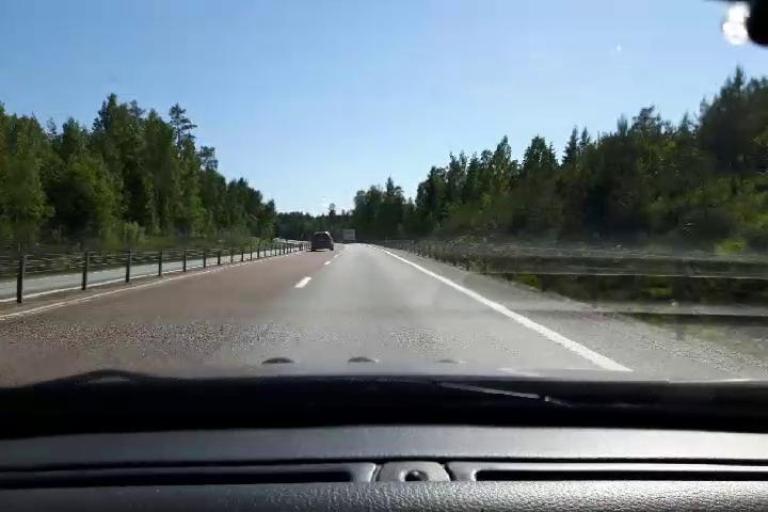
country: SE
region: Gaevleborg
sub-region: Soderhamns Kommun
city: Ljusne
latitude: 61.1325
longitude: 17.0193
